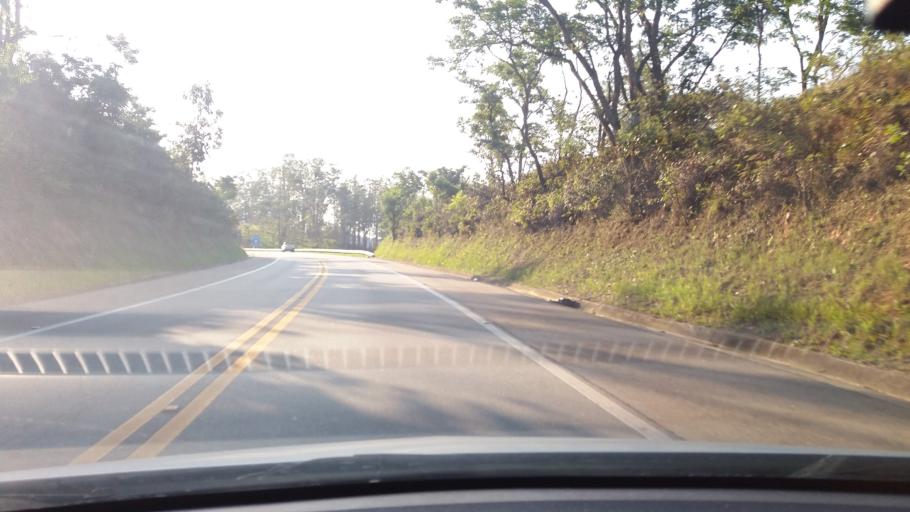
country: BR
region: Sao Paulo
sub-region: Franco Da Rocha
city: Franco da Rocha
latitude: -23.3341
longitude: -46.6670
